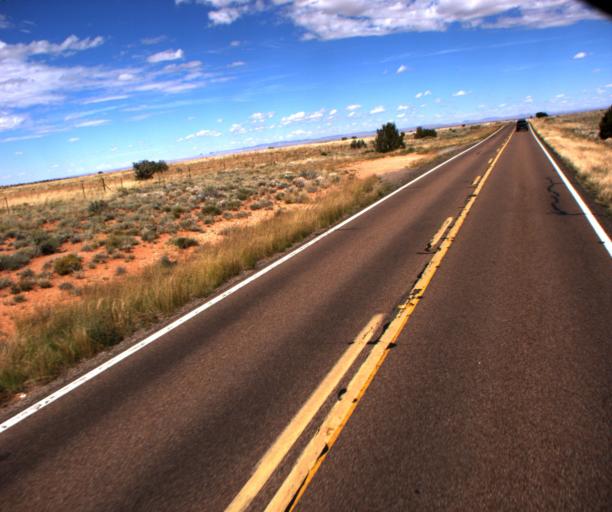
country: US
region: Arizona
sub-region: Navajo County
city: Holbrook
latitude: 34.7096
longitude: -110.2994
